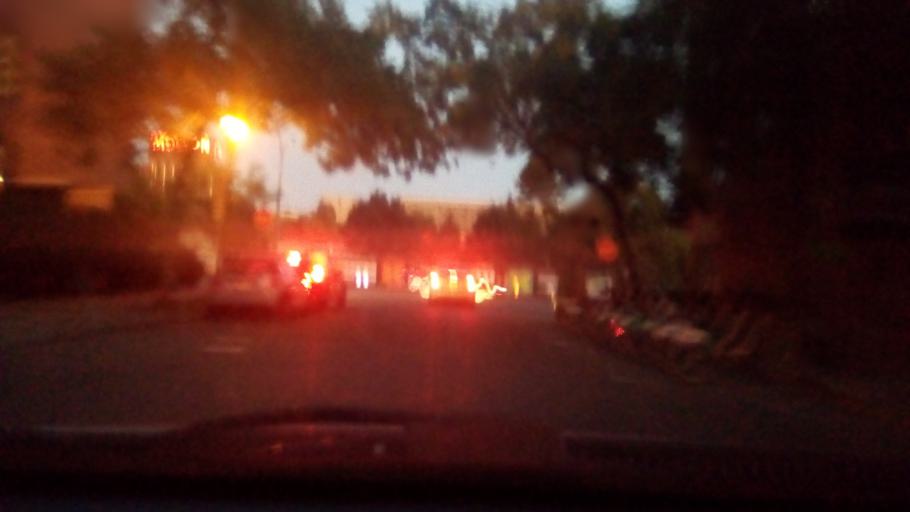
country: CA
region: Quebec
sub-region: Monteregie
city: Longueuil
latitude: 45.5195
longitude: -73.5524
